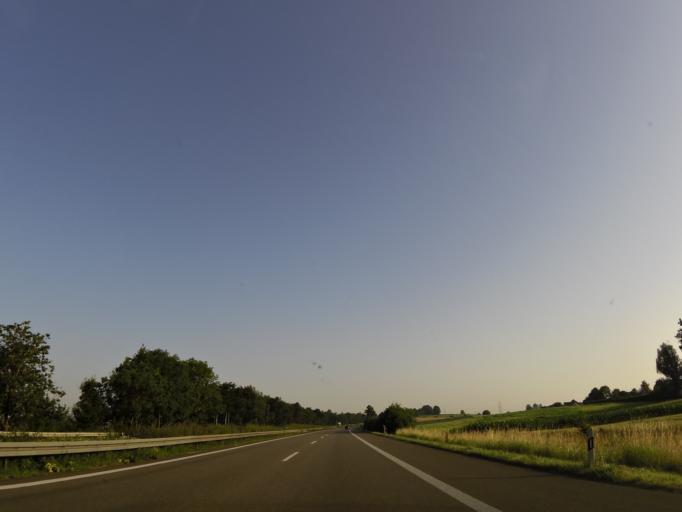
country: DE
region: Bavaria
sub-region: Swabia
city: Illertissen
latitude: 48.2449
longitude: 10.1173
